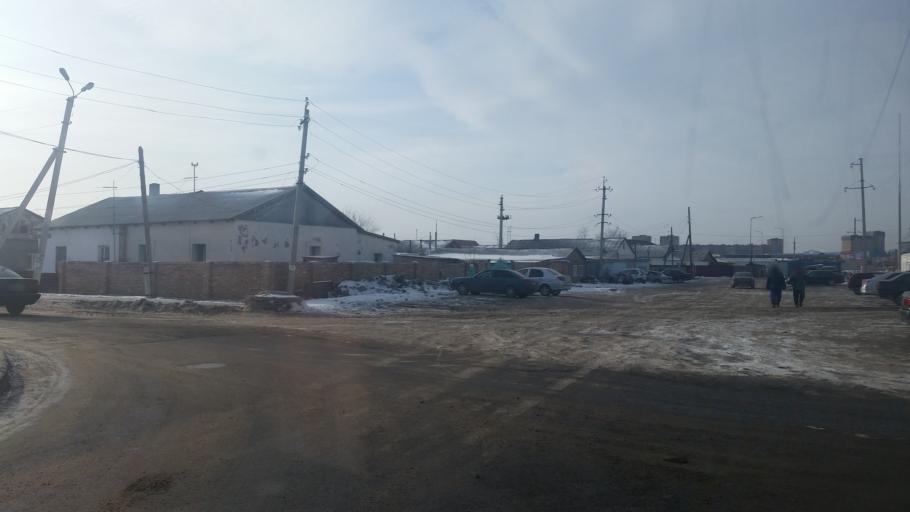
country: KZ
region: Astana Qalasy
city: Astana
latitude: 51.1837
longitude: 71.3947
